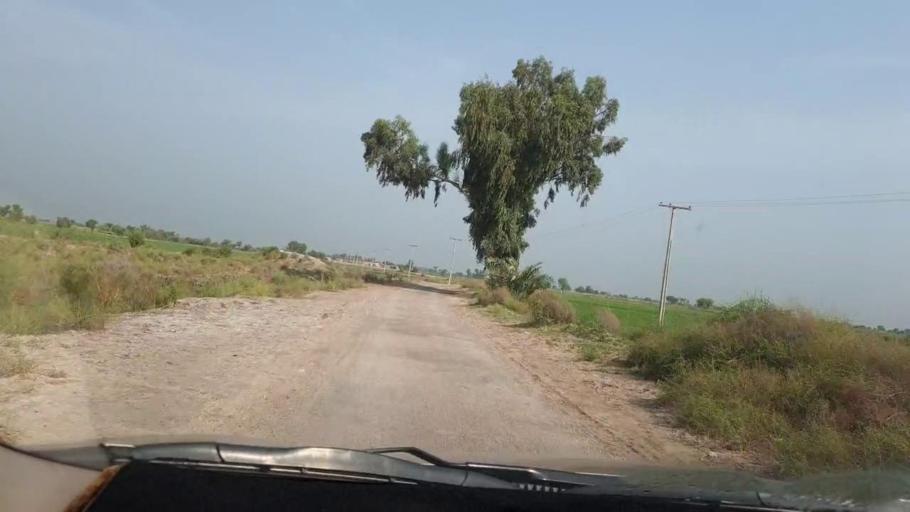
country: PK
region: Sindh
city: Goth Garelo
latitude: 27.4611
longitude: 68.0522
